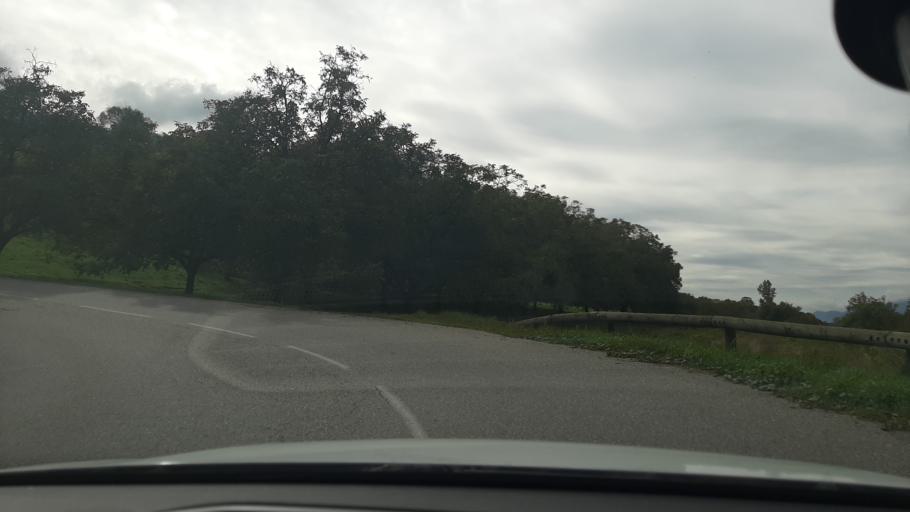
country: FR
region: Rhone-Alpes
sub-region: Departement de l'Isere
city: Pontcharra
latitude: 45.4480
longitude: 6.0510
